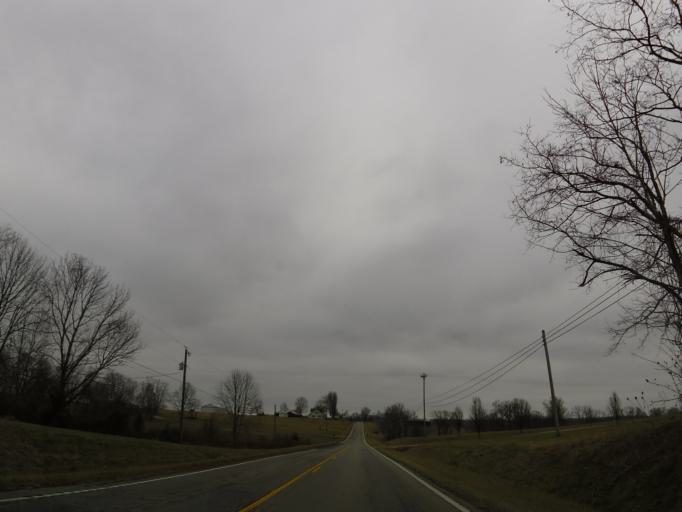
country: US
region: Kentucky
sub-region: Trimble County
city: Providence
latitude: 38.5197
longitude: -85.1886
